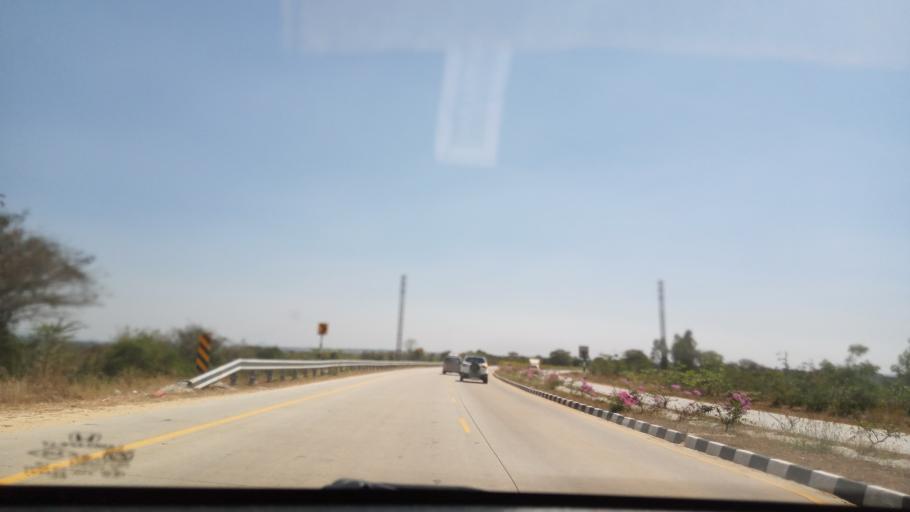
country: IN
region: Andhra Pradesh
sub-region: Chittoor
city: Palmaner
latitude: 13.1958
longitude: 78.6860
